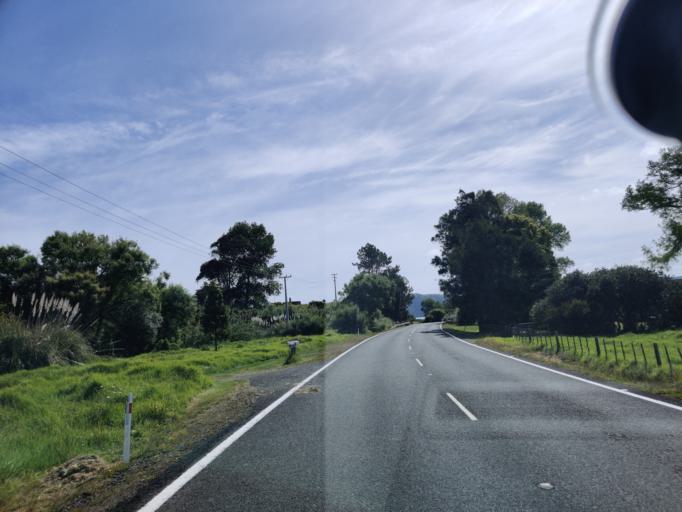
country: NZ
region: Northland
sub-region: Far North District
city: Kaitaia
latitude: -35.4958
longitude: 173.4143
